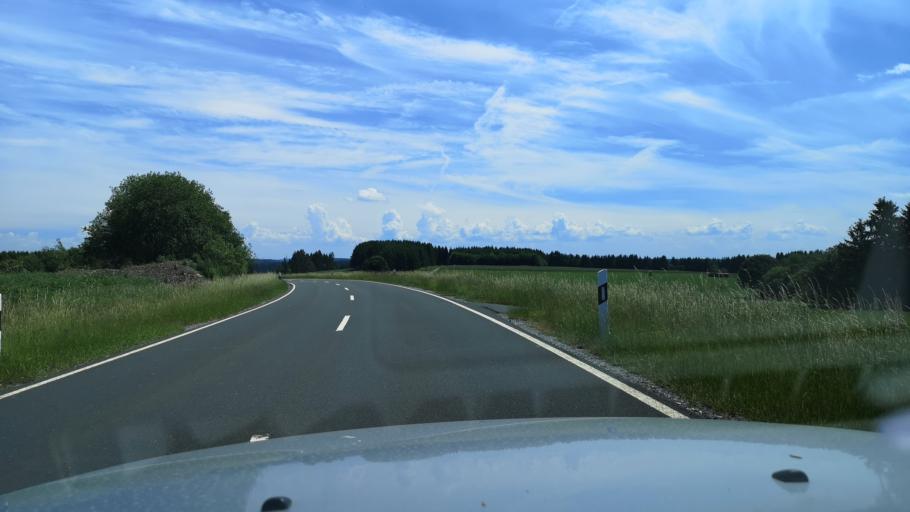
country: DE
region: Bavaria
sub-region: Upper Franconia
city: Teuschnitz
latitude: 50.3950
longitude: 11.3878
